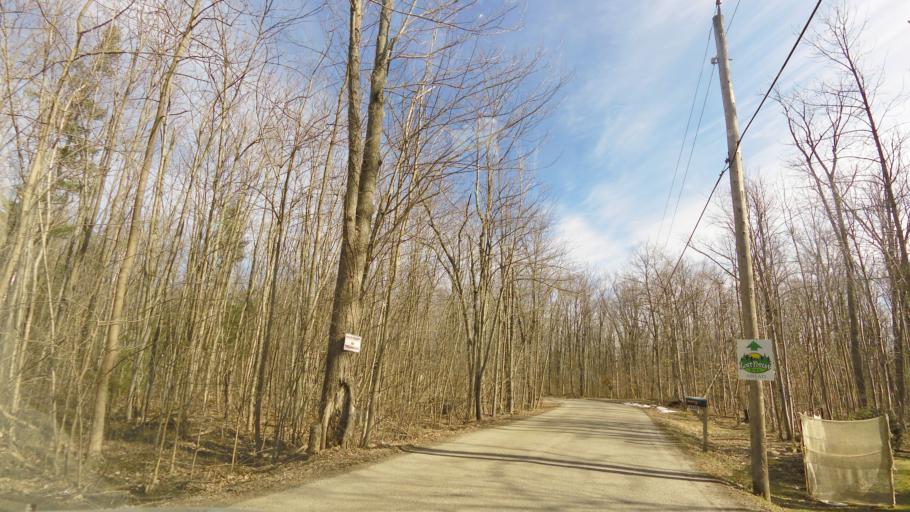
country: CA
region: Ontario
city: Burlington
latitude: 43.3793
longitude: -79.9054
